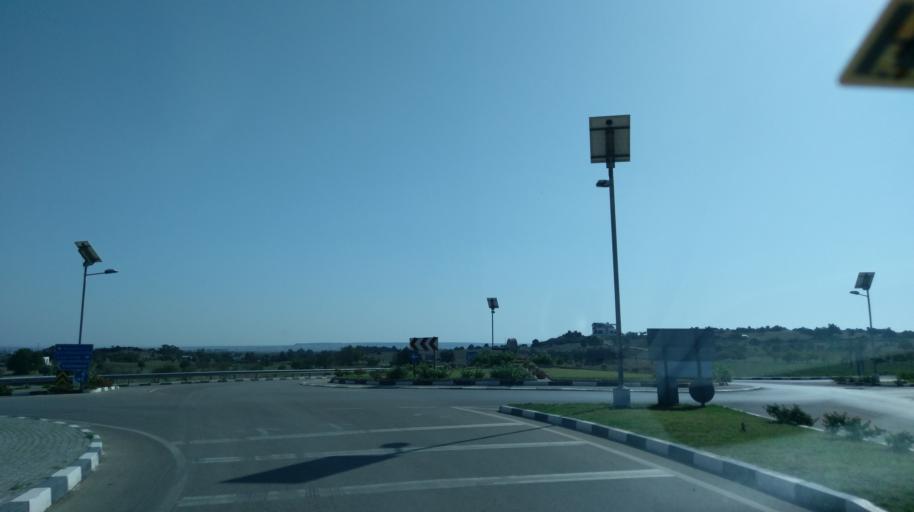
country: CY
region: Ammochostos
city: Trikomo
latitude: 35.4055
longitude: 33.9914
